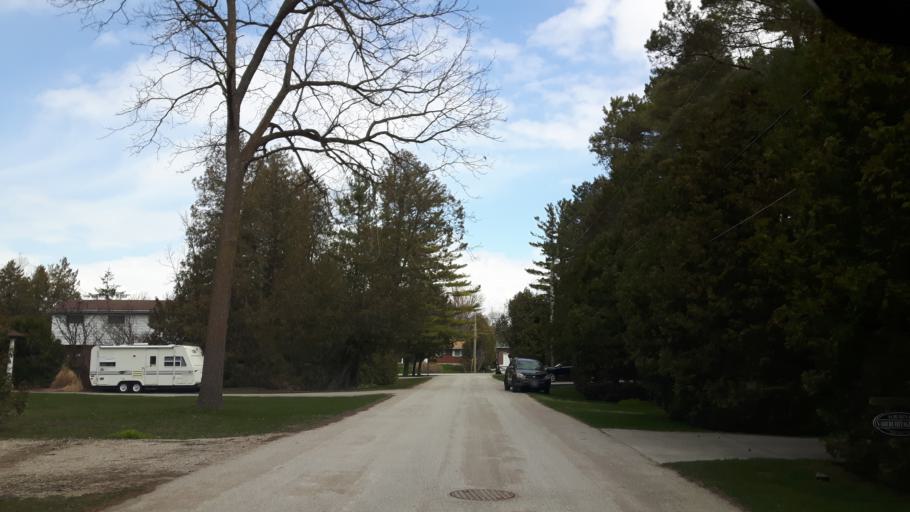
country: CA
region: Ontario
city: Bluewater
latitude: 43.5558
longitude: -81.6986
